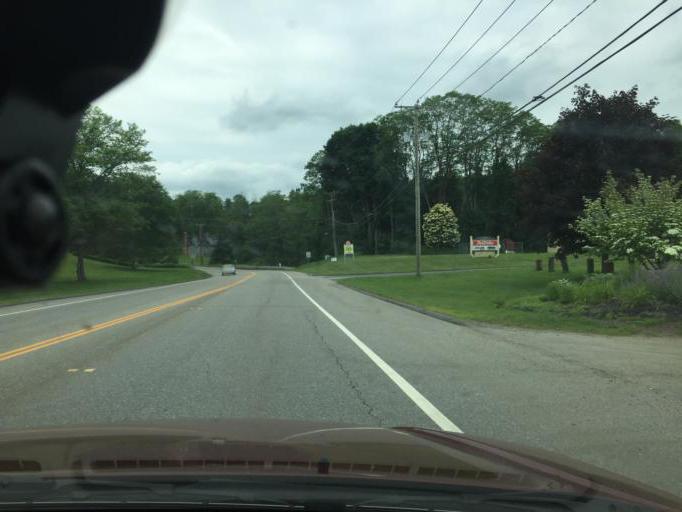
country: US
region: Connecticut
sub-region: Litchfield County
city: Litchfield
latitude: 41.7450
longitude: -73.2068
